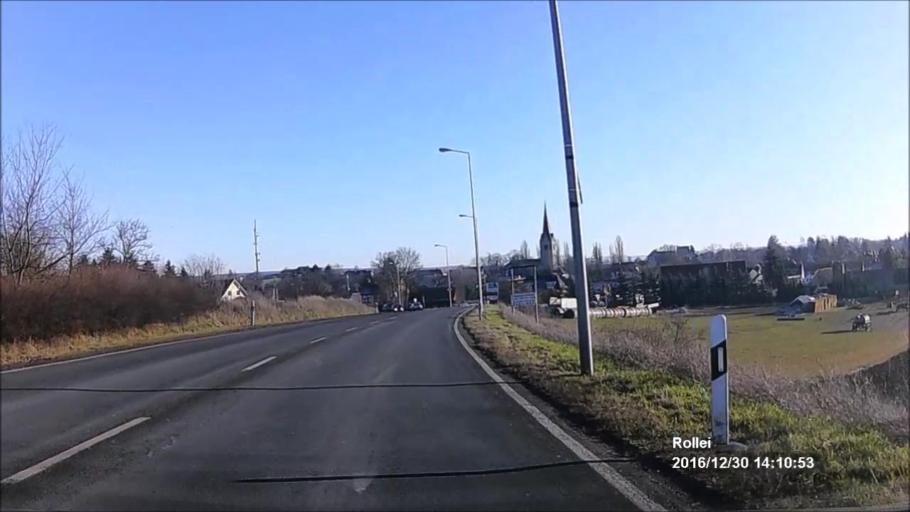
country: DE
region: Thuringia
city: Ingersleben
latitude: 50.9563
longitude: 10.9680
